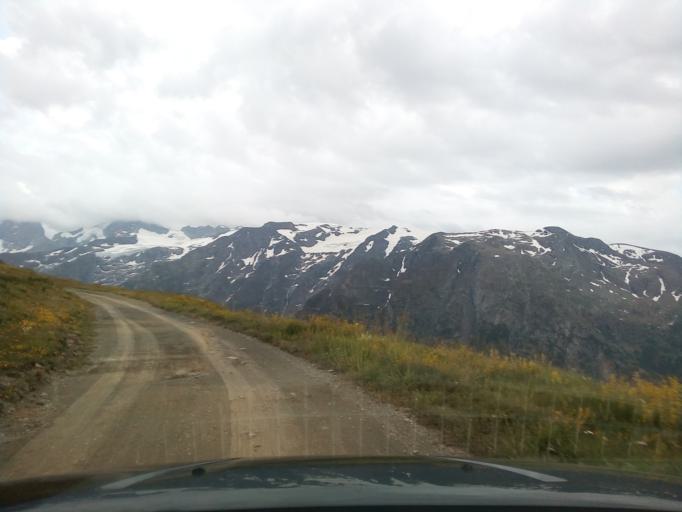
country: FR
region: Rhone-Alpes
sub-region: Departement de l'Isere
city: Mont-de-Lans
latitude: 45.0534
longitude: 6.1850
